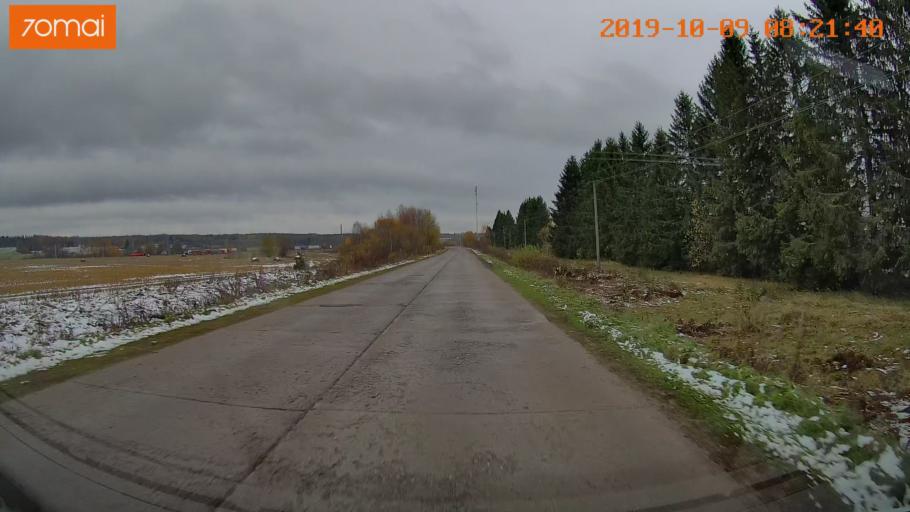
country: RU
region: Vologda
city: Gryazovets
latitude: 58.7420
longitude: 40.2809
